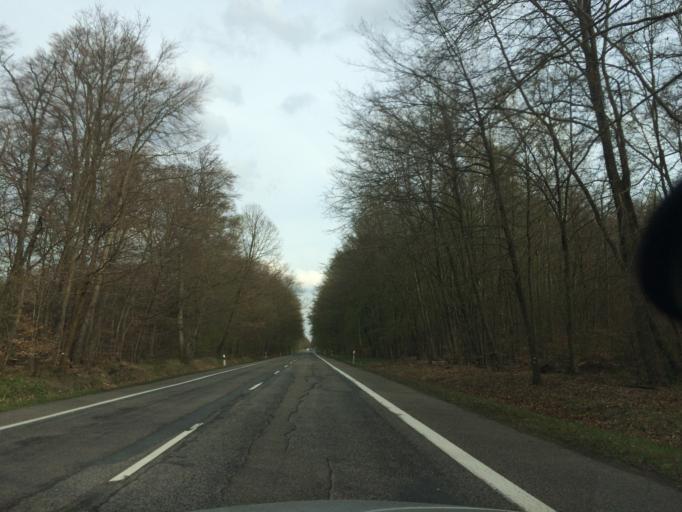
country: DE
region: Hesse
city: Langen
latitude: 50.0282
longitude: 8.6331
